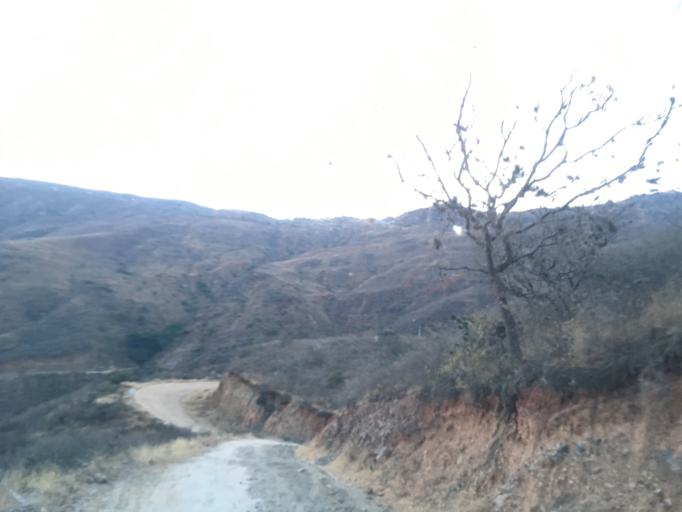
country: CO
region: Santander
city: Aratoca
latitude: 6.7932
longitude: -72.9944
